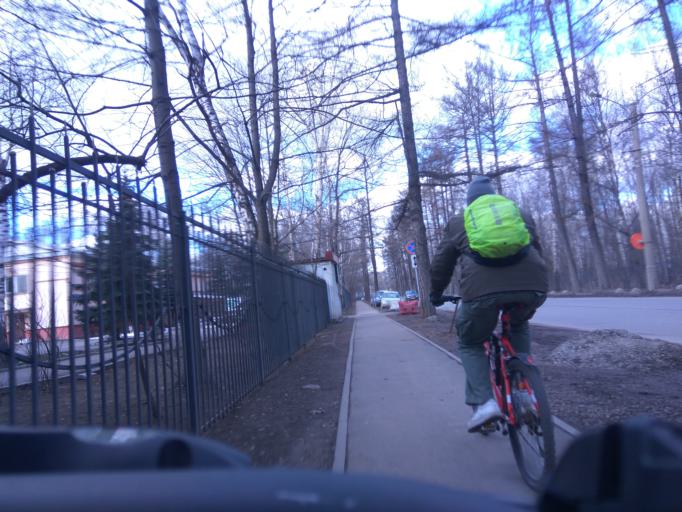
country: RU
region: Moscow
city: Sokol'niki
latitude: 55.7989
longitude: 37.6574
